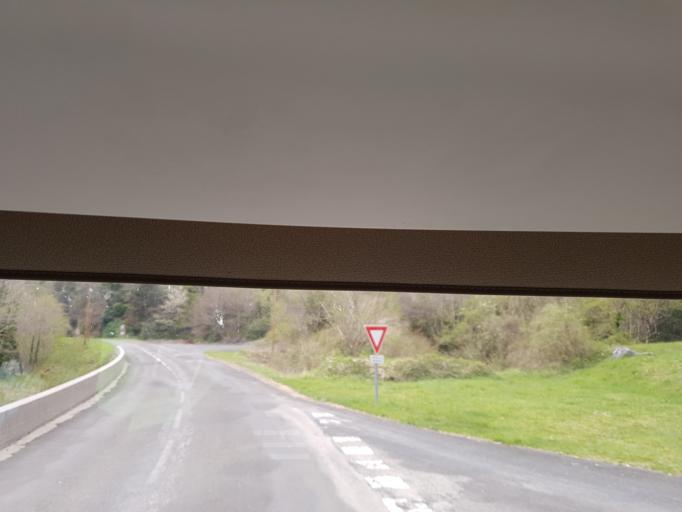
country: FR
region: Languedoc-Roussillon
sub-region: Departement de l'Aude
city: Quillan
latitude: 42.7745
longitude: 2.1815
